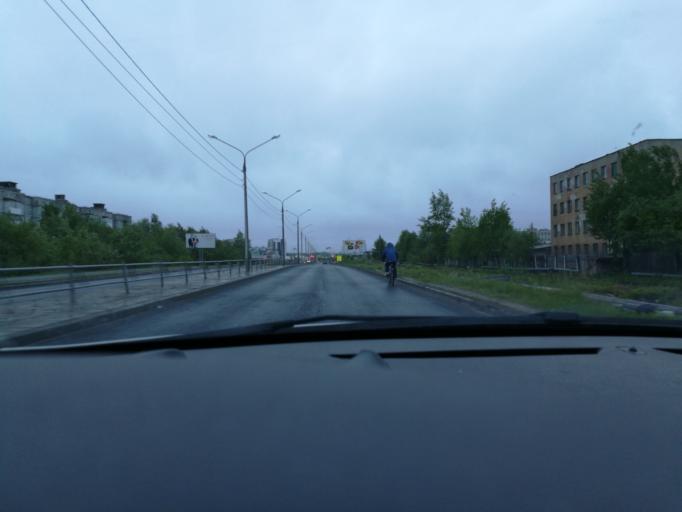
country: RU
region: Arkhangelskaya
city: Severodvinsk
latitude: 64.5652
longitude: 39.7849
